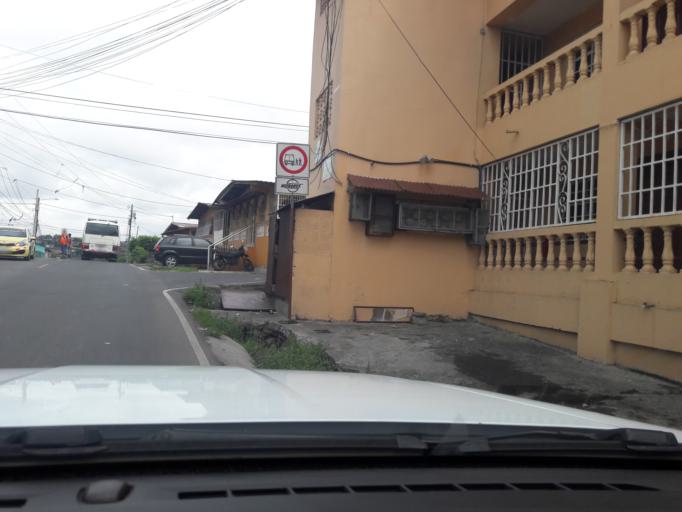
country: PA
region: Panama
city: San Miguelito
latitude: 9.0490
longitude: -79.5040
